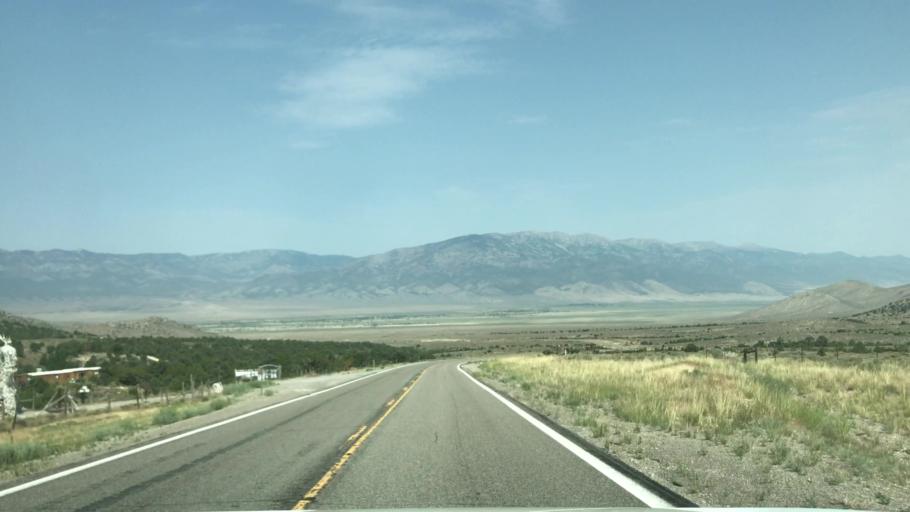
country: US
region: Nevada
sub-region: White Pine County
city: McGill
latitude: 39.1647
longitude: -114.3617
